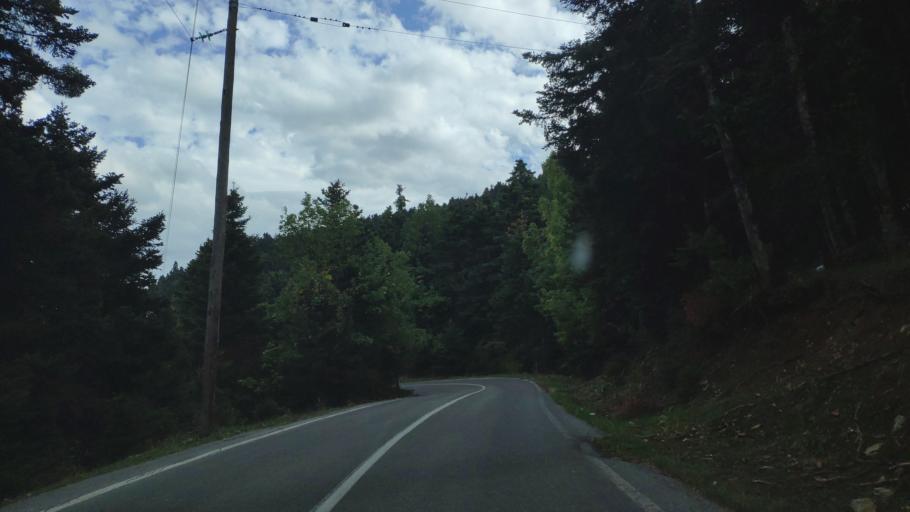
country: GR
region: Central Greece
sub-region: Nomos Fthiotidos
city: Anthili
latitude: 38.7374
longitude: 22.3747
